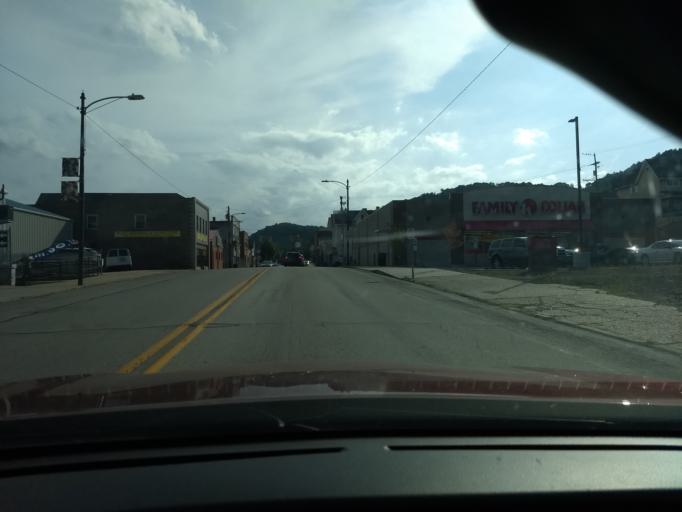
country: US
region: Pennsylvania
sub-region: Allegheny County
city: Tarentum
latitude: 40.6008
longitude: -79.7600
